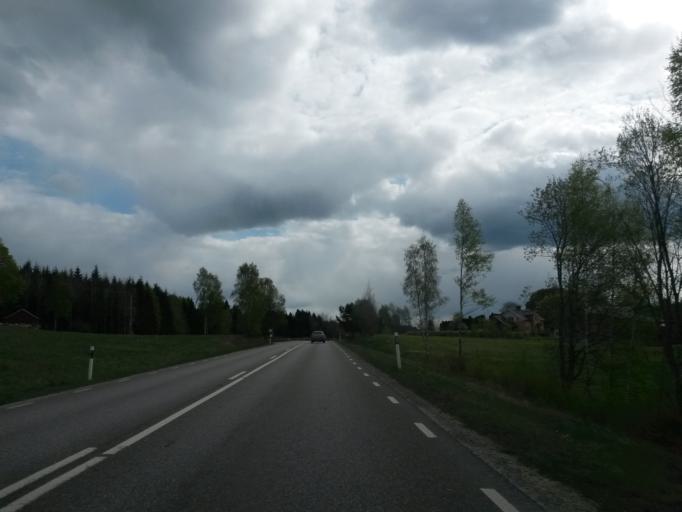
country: SE
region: Vaestra Goetaland
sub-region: Vargarda Kommun
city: Vargarda
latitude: 57.9624
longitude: 12.8138
